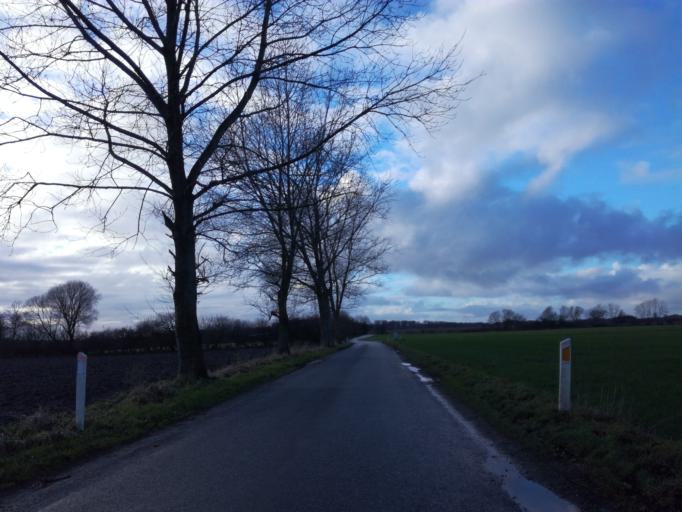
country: DK
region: South Denmark
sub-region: Fredericia Kommune
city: Taulov
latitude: 55.5633
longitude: 9.6556
